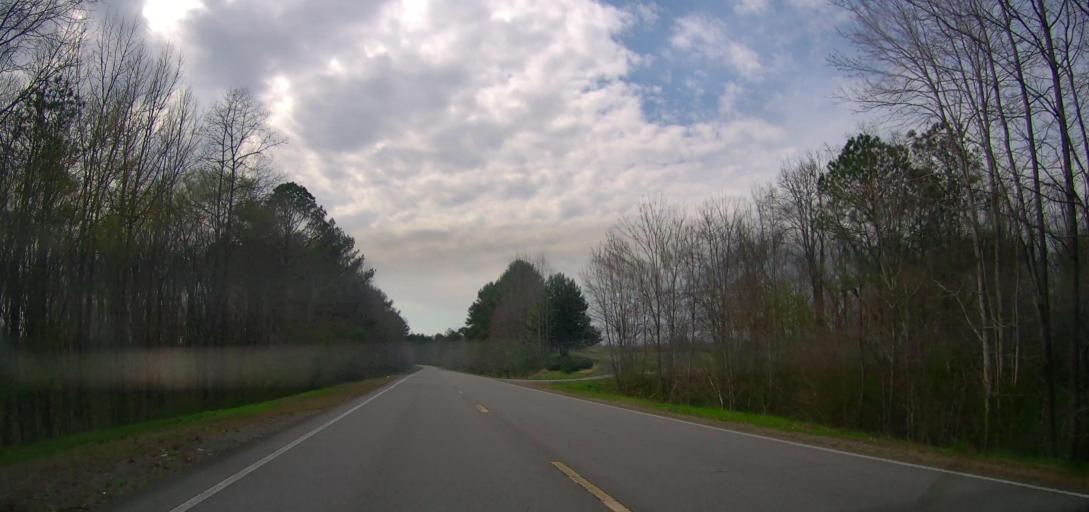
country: US
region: Alabama
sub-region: Marion County
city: Winfield
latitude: 33.9351
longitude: -87.7177
